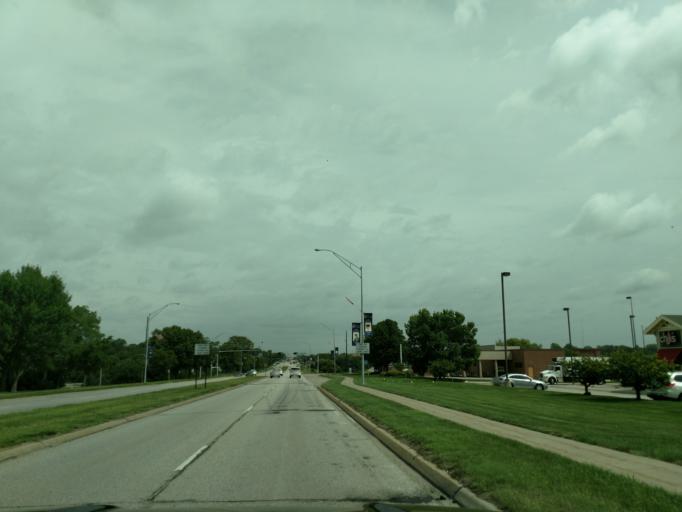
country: US
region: Nebraska
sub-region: Sarpy County
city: La Vista
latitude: 41.1820
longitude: -96.0430
